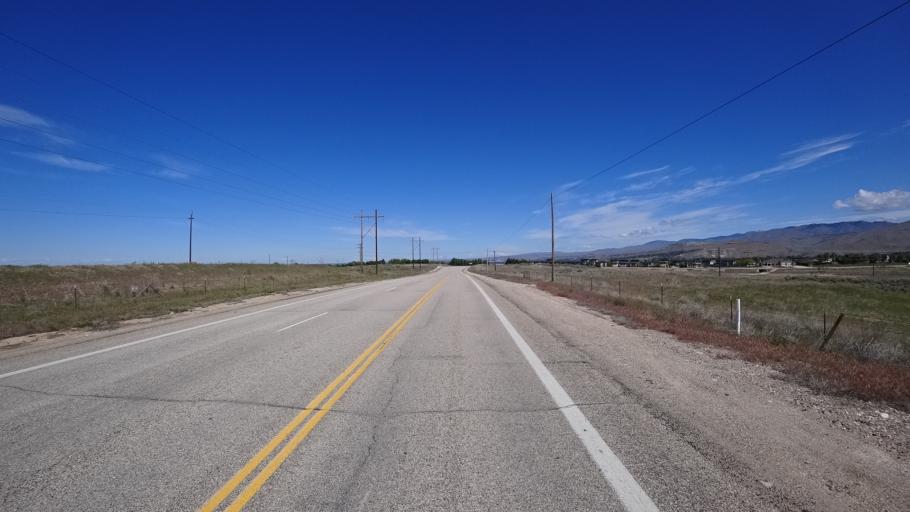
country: US
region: Idaho
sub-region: Ada County
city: Boise
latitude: 43.5370
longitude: -116.1451
